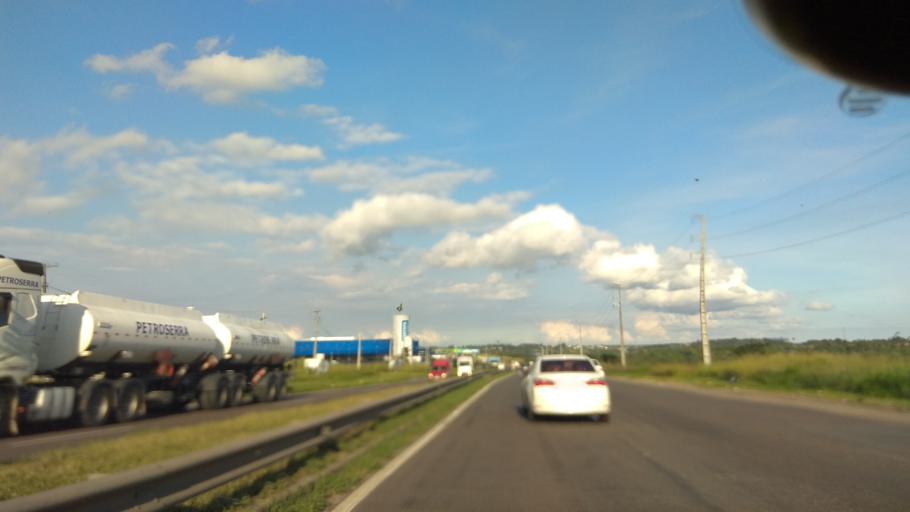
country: BR
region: Bahia
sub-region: Conceicao Do Jacuipe
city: Conceicao do Jacuipe
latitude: -12.3401
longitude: -38.8460
